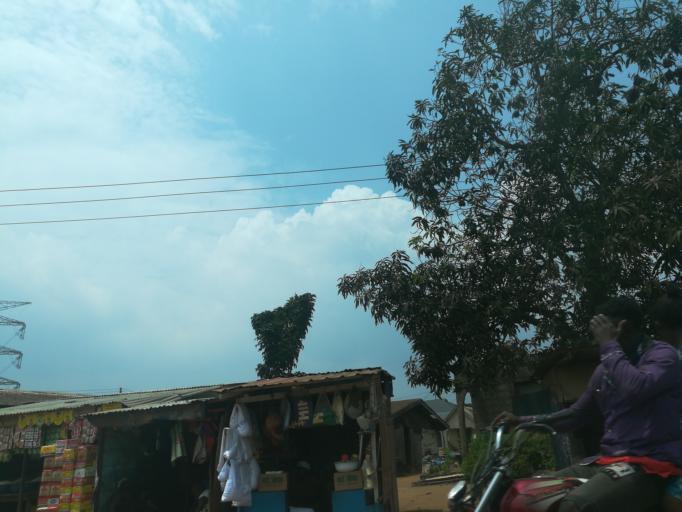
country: NG
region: Lagos
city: Ikorodu
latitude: 6.6076
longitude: 3.5907
